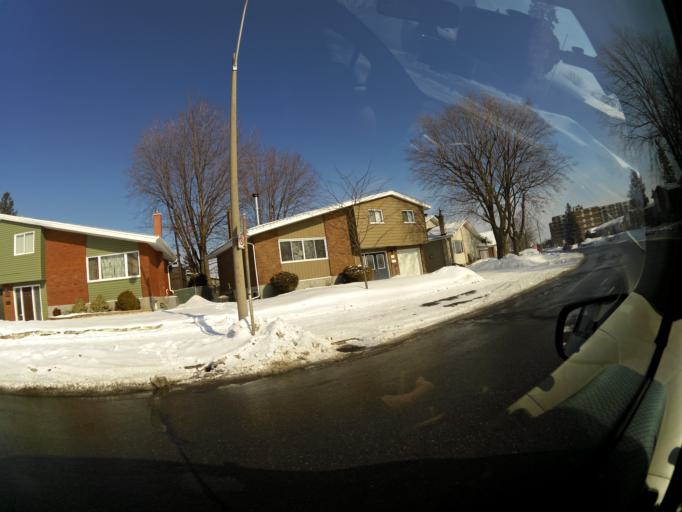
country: CA
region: Ontario
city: Ottawa
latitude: 45.3891
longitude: -75.6343
